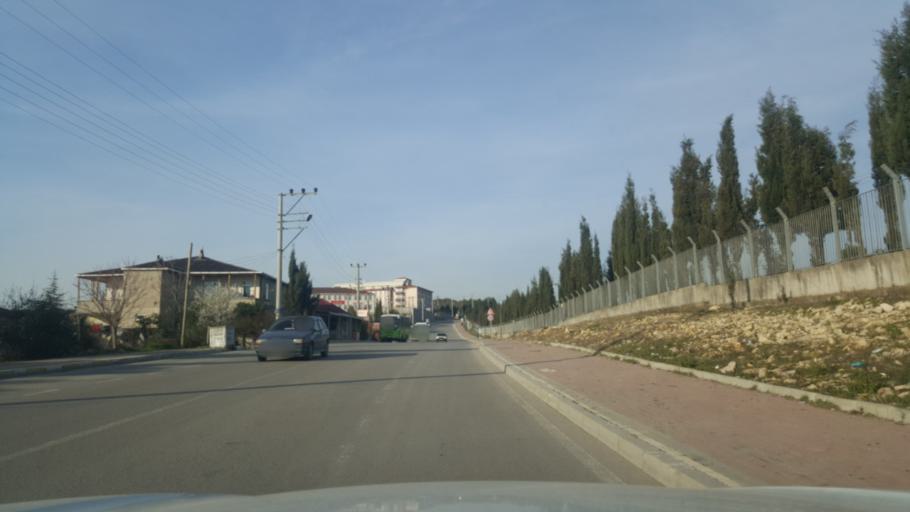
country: TR
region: Kocaeli
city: Tavsancil
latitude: 40.7937
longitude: 29.5514
